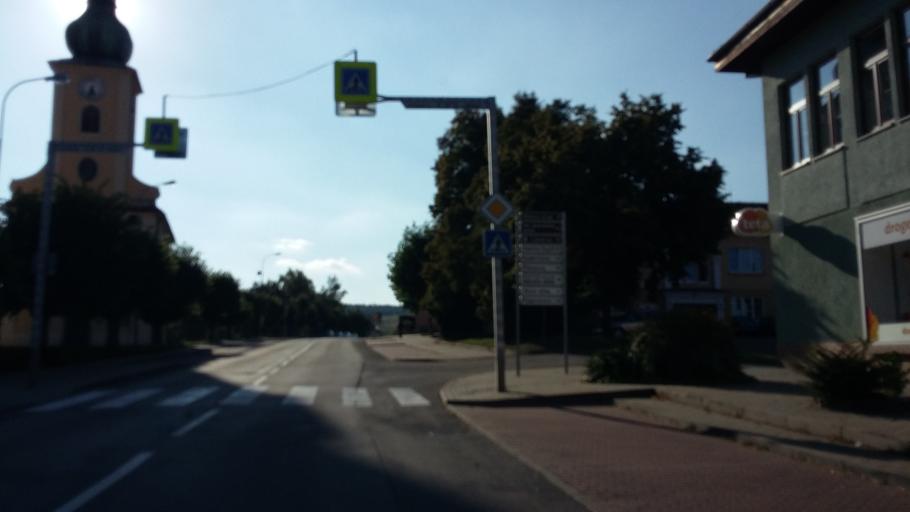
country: CZ
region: South Moravian
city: Ricany
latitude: 49.2149
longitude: 16.3940
